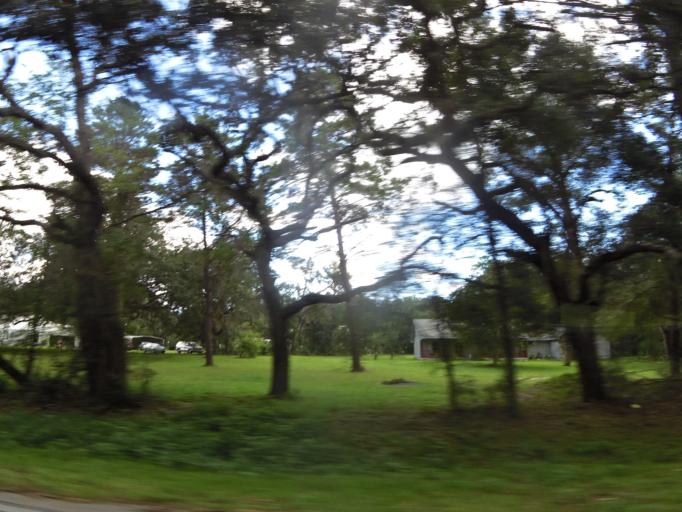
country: US
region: Florida
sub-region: Putnam County
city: East Palatka
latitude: 29.7731
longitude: -81.4819
